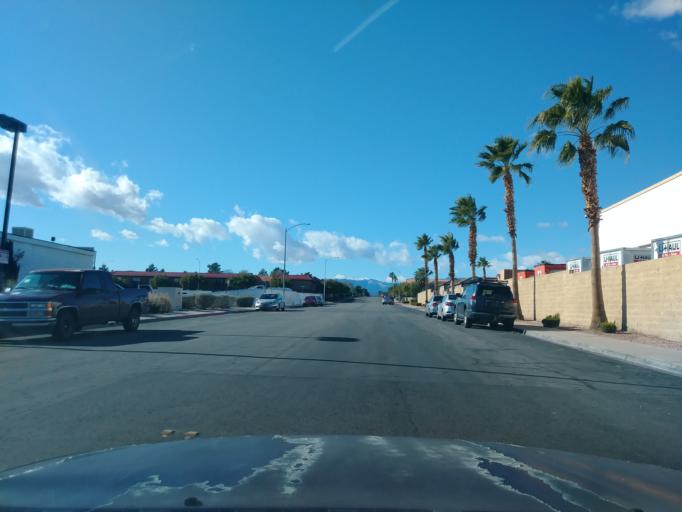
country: US
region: Nevada
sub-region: Clark County
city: Spring Valley
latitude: 36.1500
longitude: -115.2089
